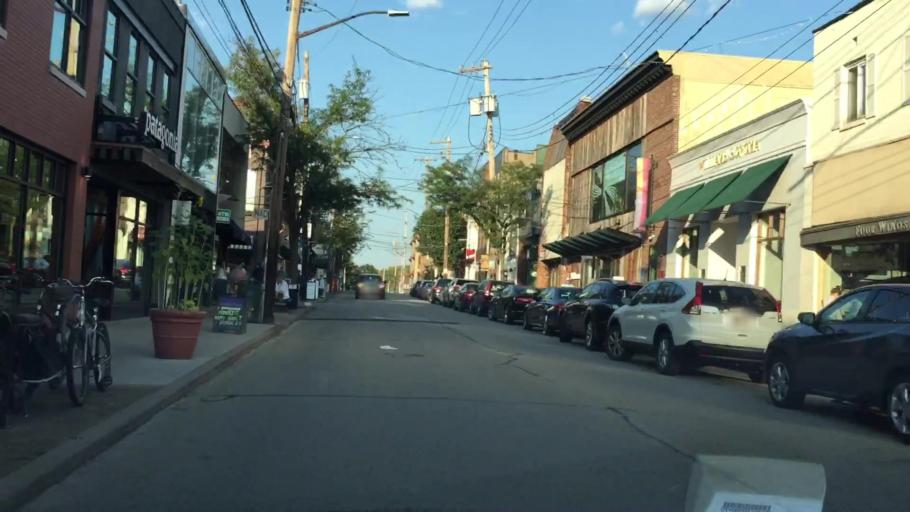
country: US
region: Pennsylvania
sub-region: Allegheny County
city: Bloomfield
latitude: 40.4513
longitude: -79.9335
